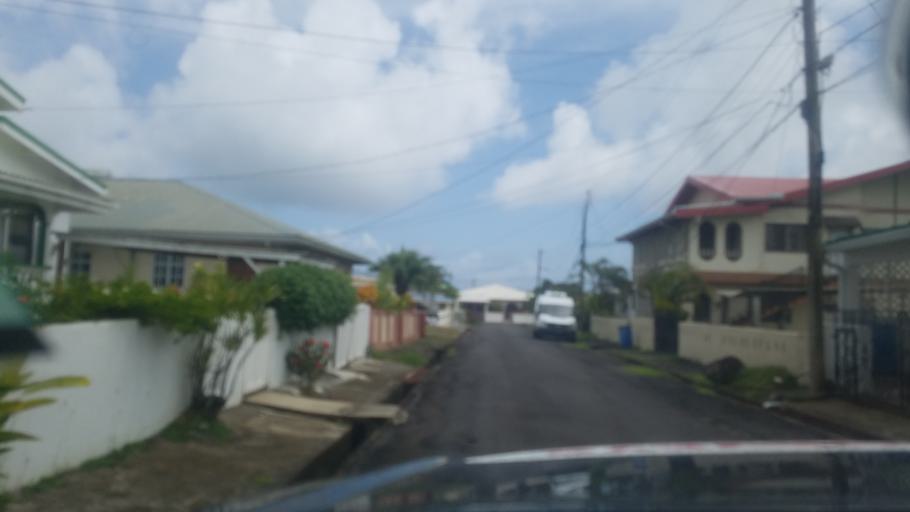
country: LC
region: Laborie Quarter
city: Laborie
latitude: 13.7449
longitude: -60.9751
